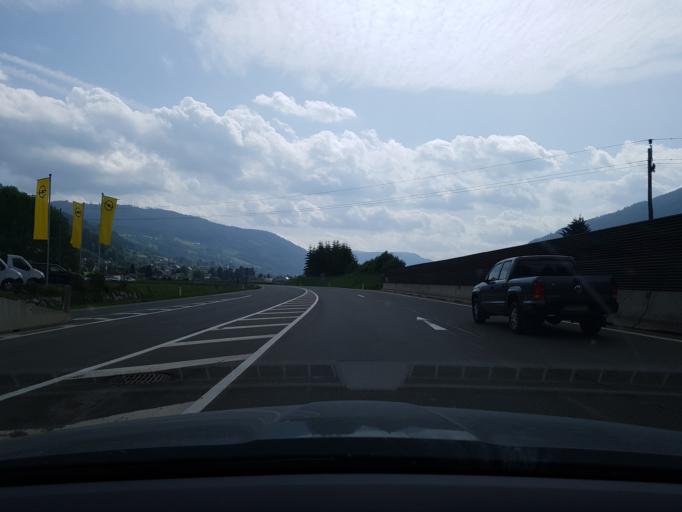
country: AT
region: Salzburg
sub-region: Politischer Bezirk Tamsweg
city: Sankt Michael im Lungau
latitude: 47.0957
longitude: 13.6143
